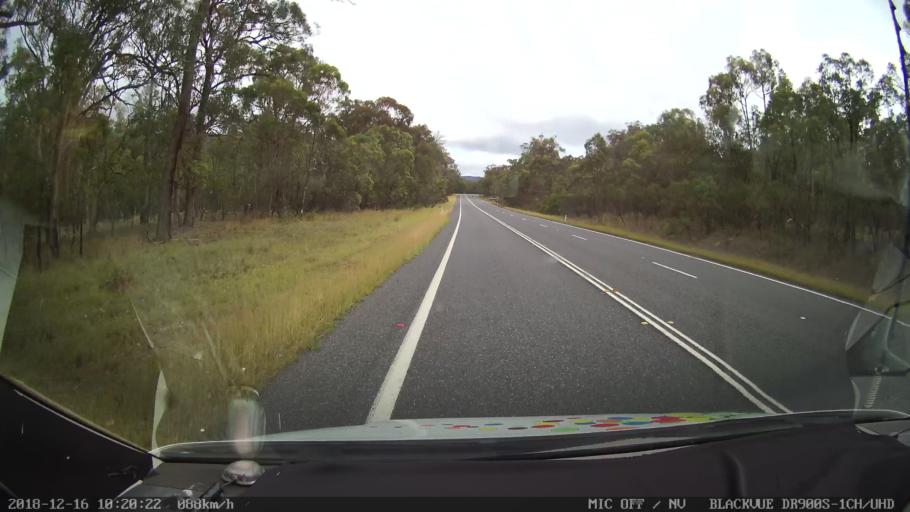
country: AU
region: New South Wales
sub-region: Tenterfield Municipality
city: Carrolls Creek
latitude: -29.2209
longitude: 152.0098
